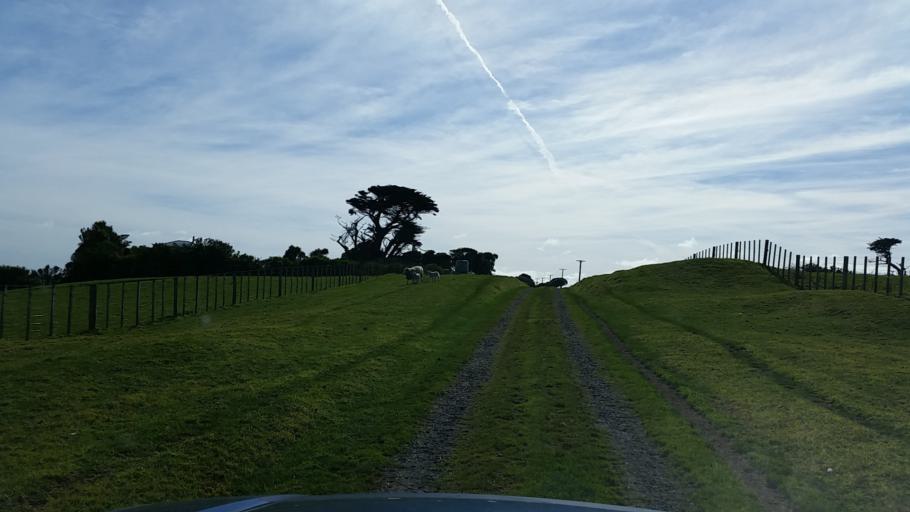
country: NZ
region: Taranaki
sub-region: South Taranaki District
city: Patea
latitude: -39.7705
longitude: 174.4939
